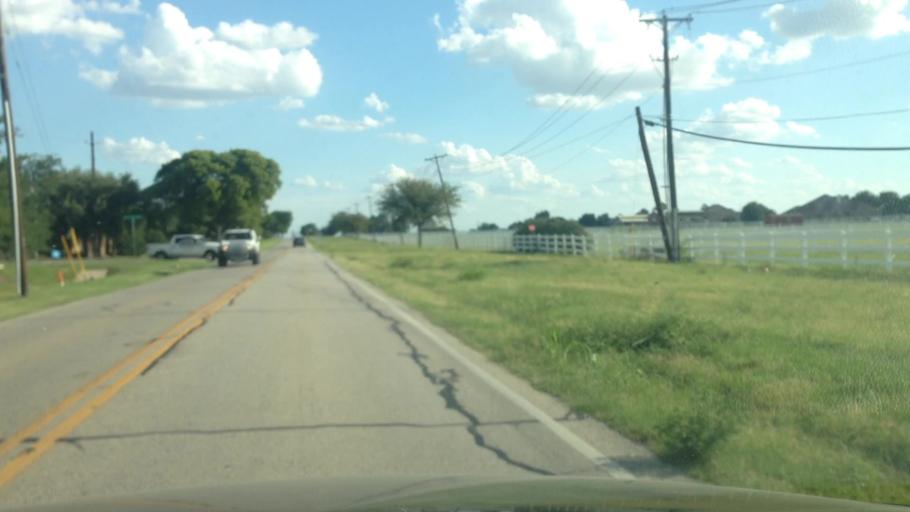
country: US
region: Texas
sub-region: Tarrant County
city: Haslet
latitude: 32.9229
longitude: -97.3749
